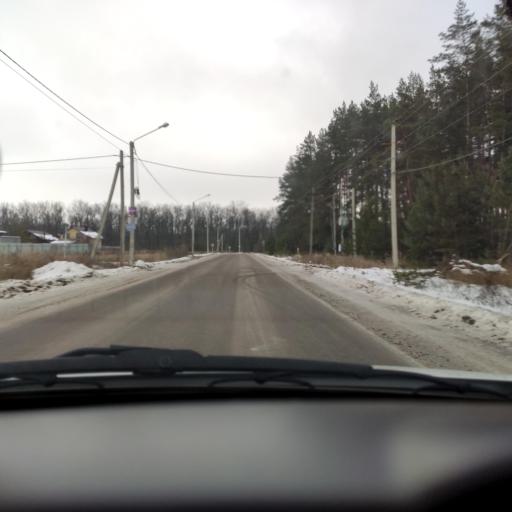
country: RU
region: Voronezj
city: Ramon'
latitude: 51.8940
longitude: 39.2754
